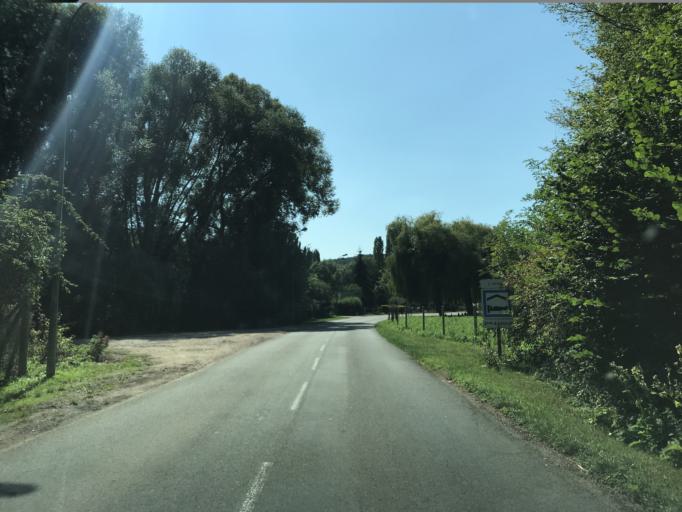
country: FR
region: Haute-Normandie
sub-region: Departement de l'Eure
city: Houlbec-Cocherel
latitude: 49.0694
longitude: 1.2952
